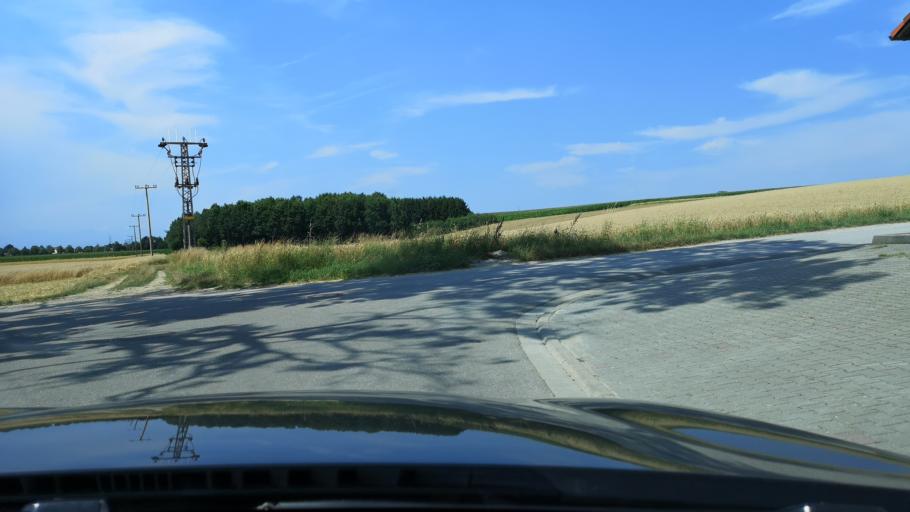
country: DE
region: Bavaria
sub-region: Upper Bavaria
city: Pliening
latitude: 48.1860
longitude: 11.8114
